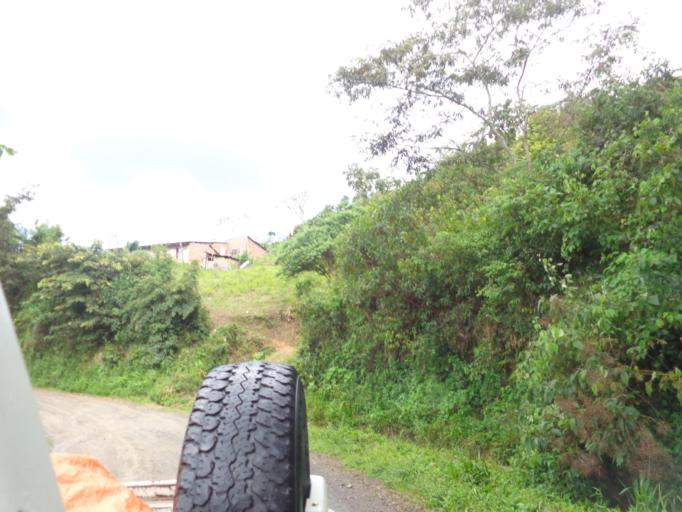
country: BO
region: La Paz
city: Coroico
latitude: -16.1294
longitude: -67.7530
